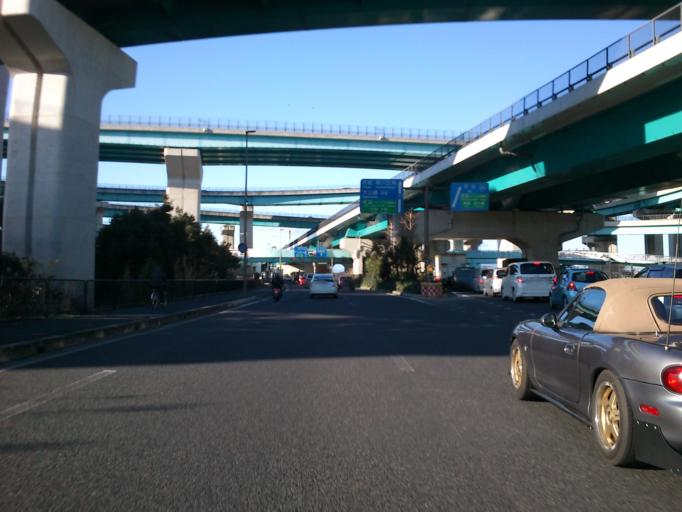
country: JP
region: Kyoto
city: Yawata
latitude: 34.8956
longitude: 135.7489
